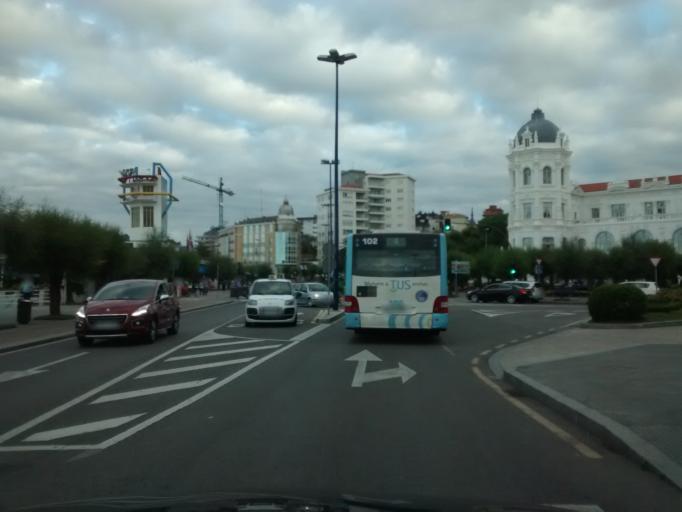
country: ES
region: Cantabria
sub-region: Provincia de Cantabria
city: Santander
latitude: 43.4727
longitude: -3.7829
